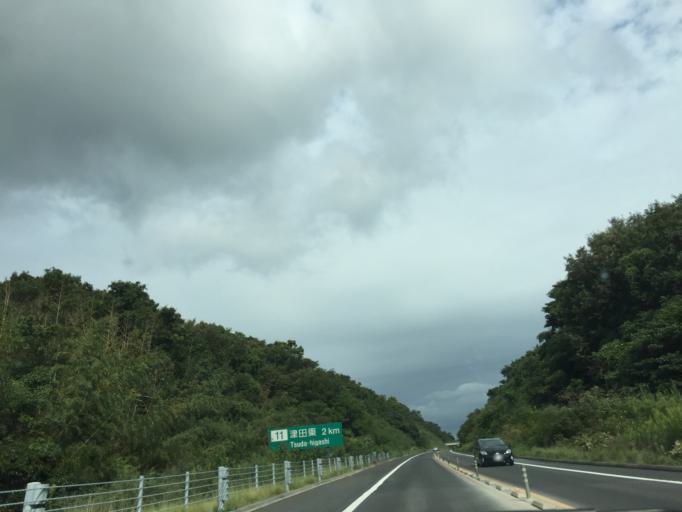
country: JP
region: Kagawa
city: Shido
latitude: 34.2604
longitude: 134.2880
